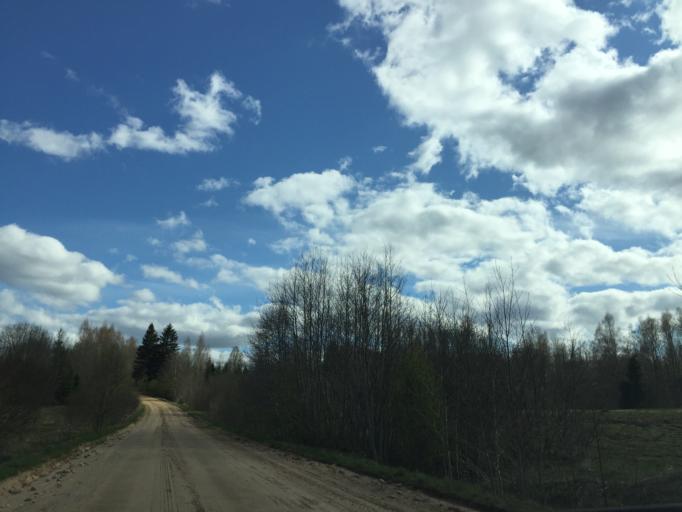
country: LV
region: Rezekne
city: Rezekne
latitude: 56.6357
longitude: 27.2997
